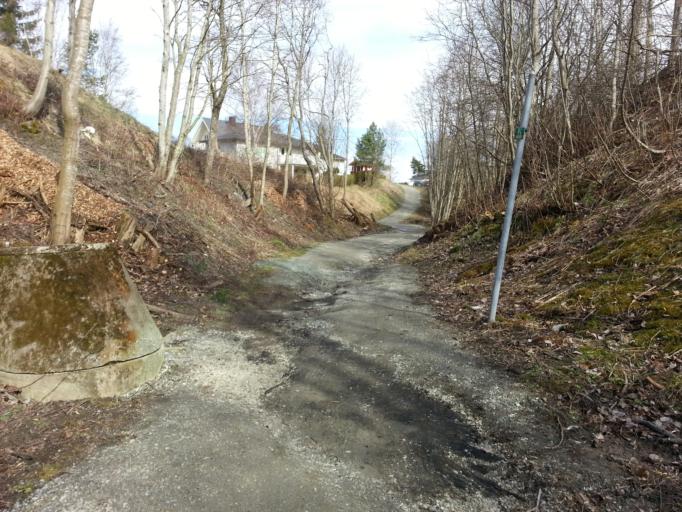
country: NO
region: Sor-Trondelag
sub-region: Trondheim
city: Trondheim
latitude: 63.4203
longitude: 10.4438
